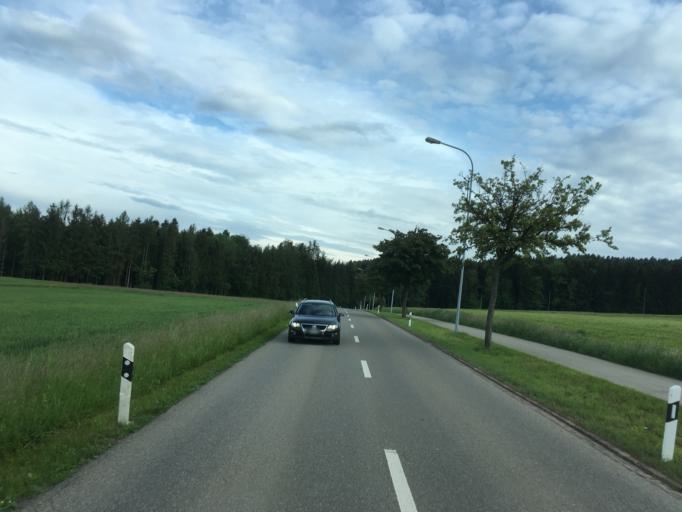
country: CH
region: Zurich
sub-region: Bezirk Uster
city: Ebmatingen
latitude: 47.3469
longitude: 8.6455
